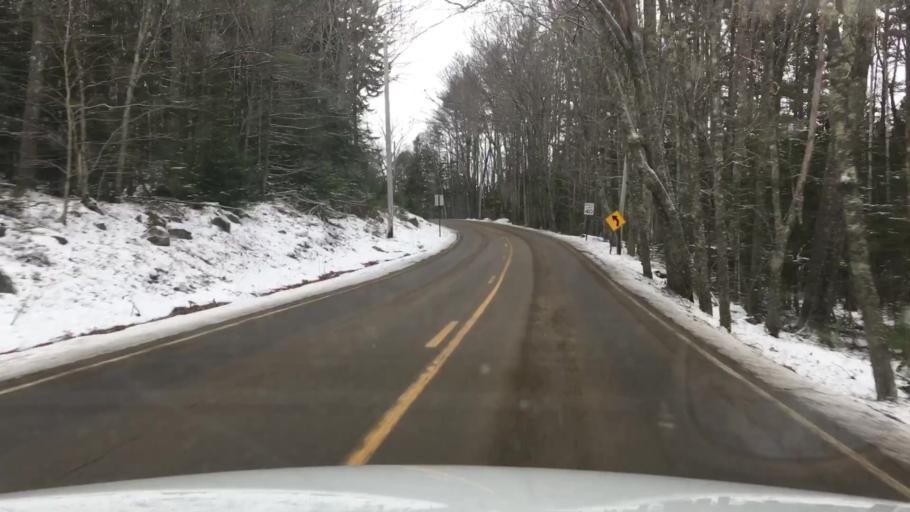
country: US
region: Maine
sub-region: Waldo County
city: Lincolnville
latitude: 44.2861
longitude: -69.0164
